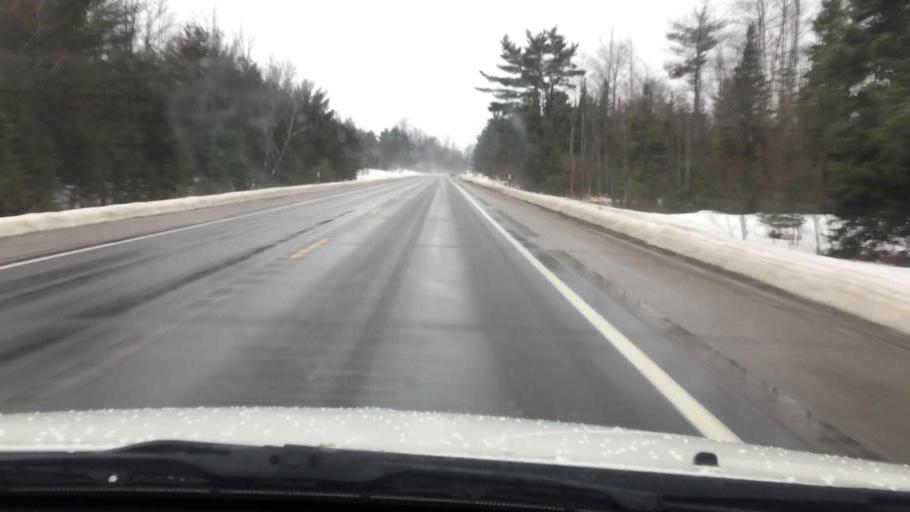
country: US
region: Michigan
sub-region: Kalkaska County
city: Kalkaska
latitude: 44.6507
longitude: -85.2678
